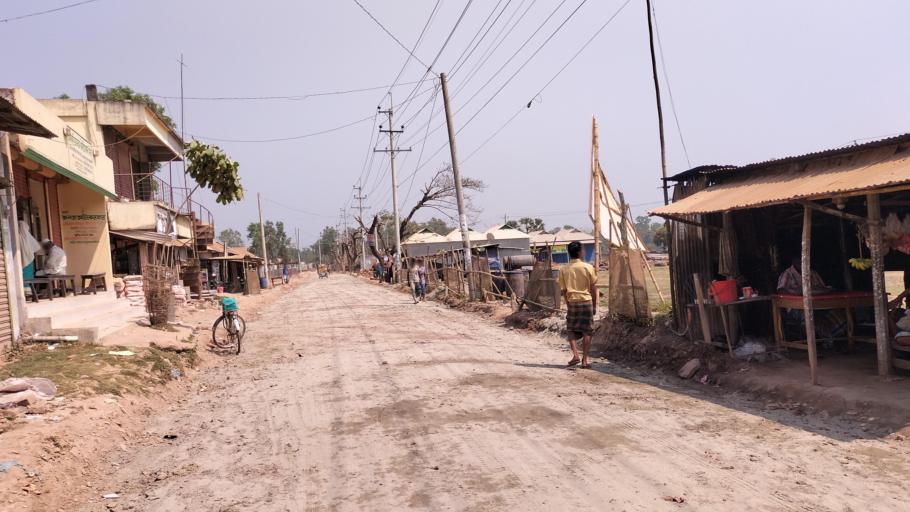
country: BD
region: Dhaka
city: Sakhipur
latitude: 24.3078
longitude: 90.3189
